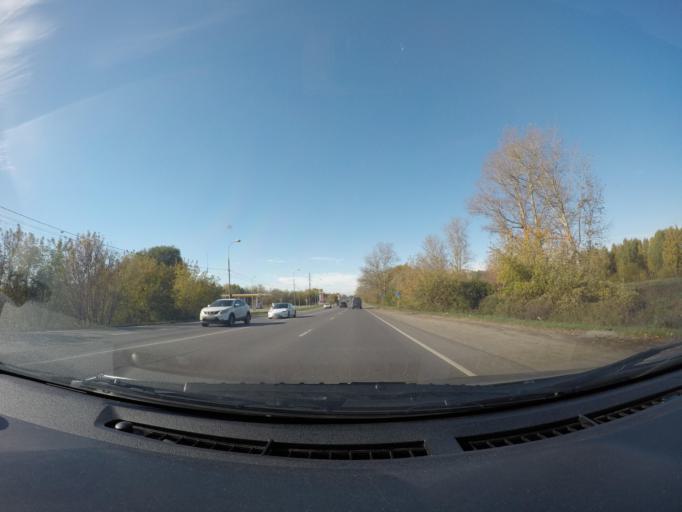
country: RU
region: Moskovskaya
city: Tomilino
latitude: 55.6336
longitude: 37.9627
